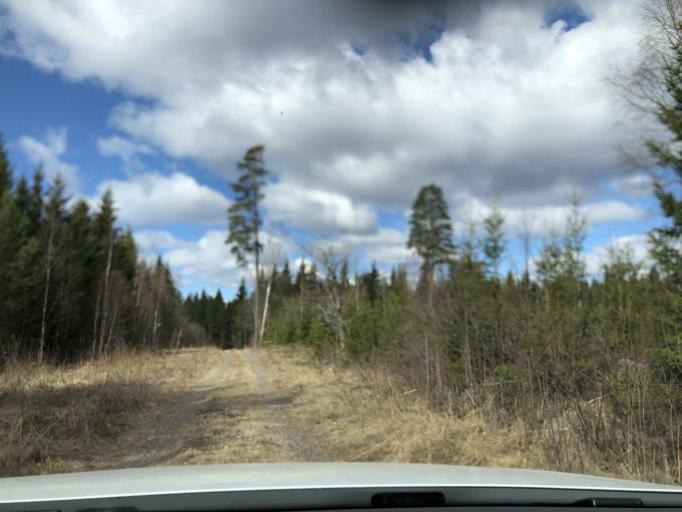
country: SE
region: Uppsala
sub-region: Tierps Kommun
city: Tierp
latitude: 60.3320
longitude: 17.3359
